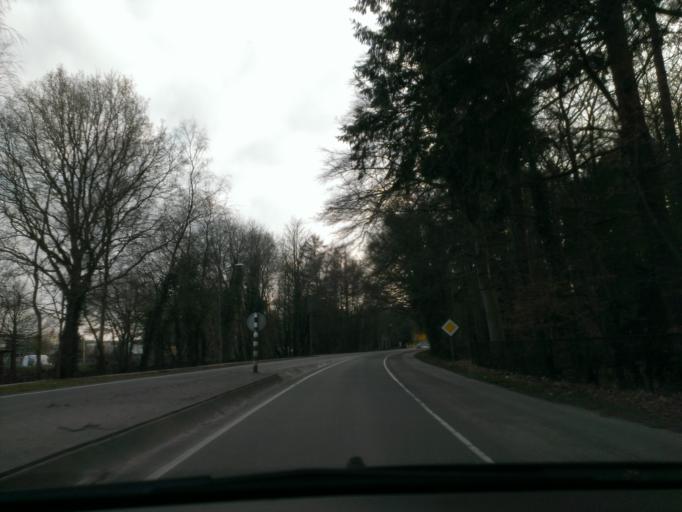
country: NL
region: Gelderland
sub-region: Gemeente Hattem
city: Hattem
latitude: 52.4376
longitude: 6.0708
